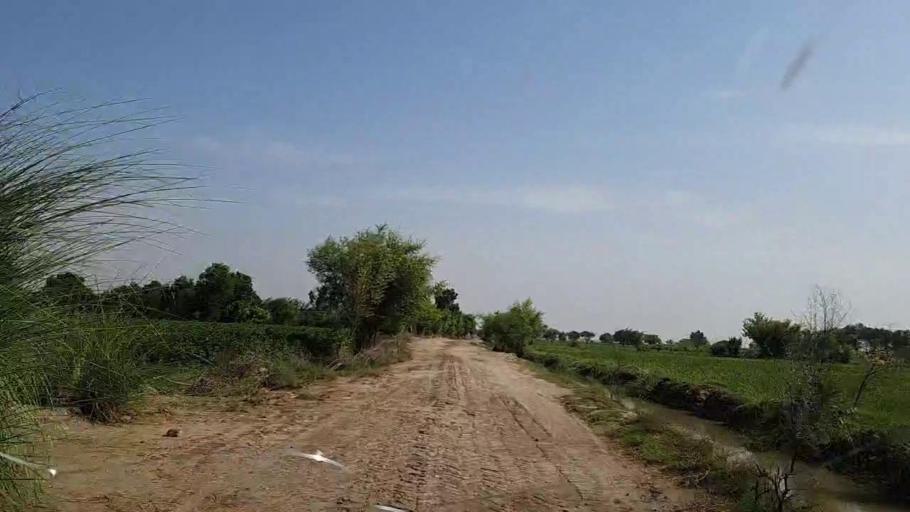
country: PK
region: Sindh
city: Khanpur
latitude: 27.6938
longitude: 69.3670
